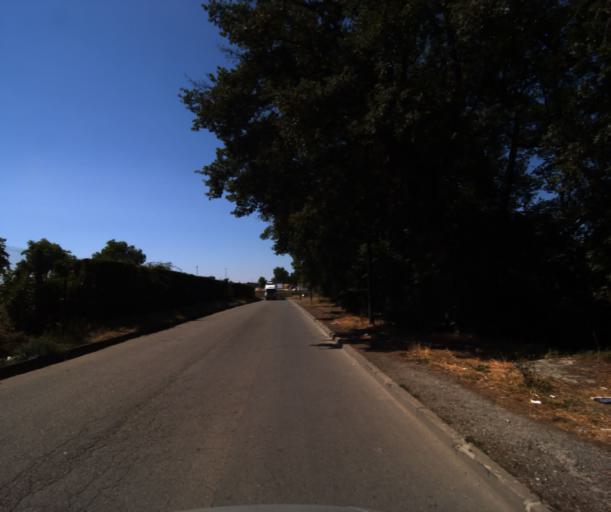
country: FR
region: Midi-Pyrenees
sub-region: Departement de la Haute-Garonne
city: Saubens
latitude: 43.4831
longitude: 1.3399
